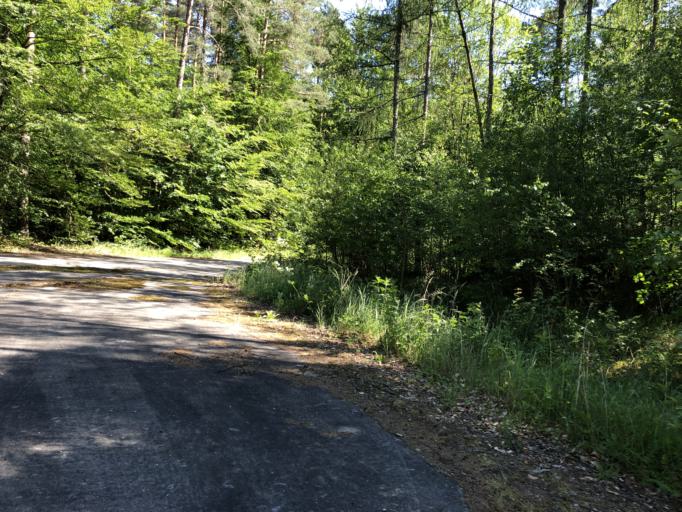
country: DE
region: Bavaria
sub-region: Upper Franconia
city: Memmelsdorf
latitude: 49.9135
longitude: 10.9611
